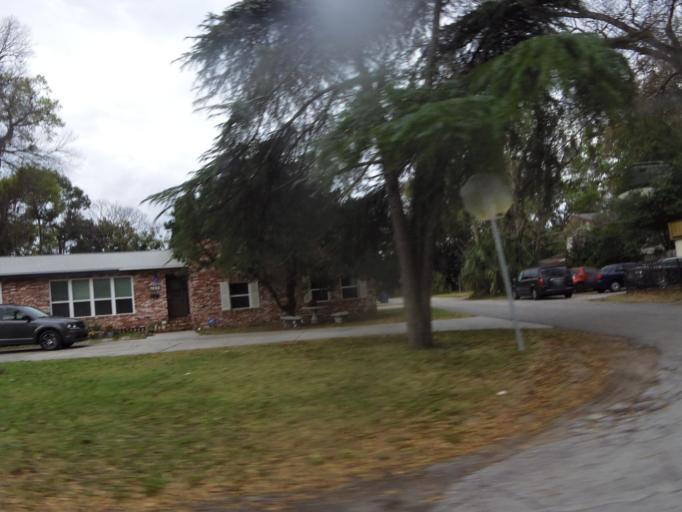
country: US
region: Florida
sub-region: Duval County
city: Jacksonville
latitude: 30.3409
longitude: -81.6066
